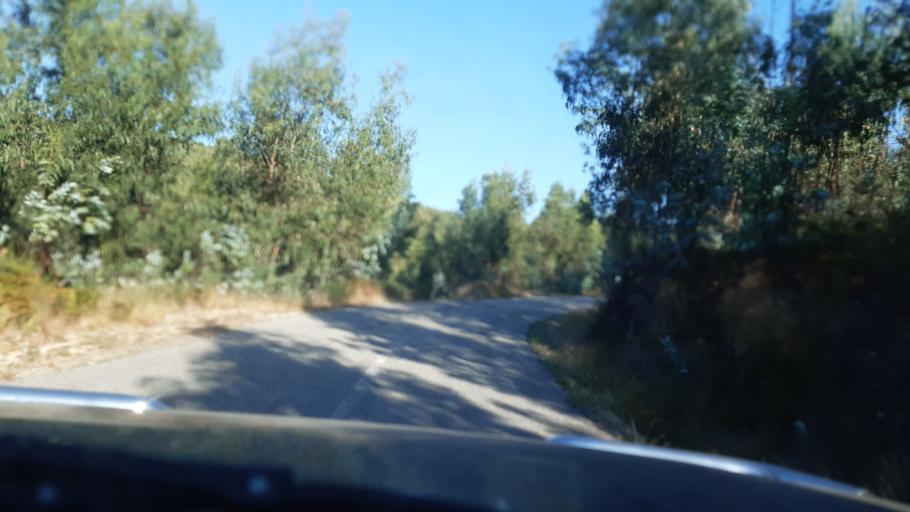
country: PT
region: Aveiro
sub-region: Agueda
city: Aguada de Cima
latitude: 40.5647
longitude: -8.3431
